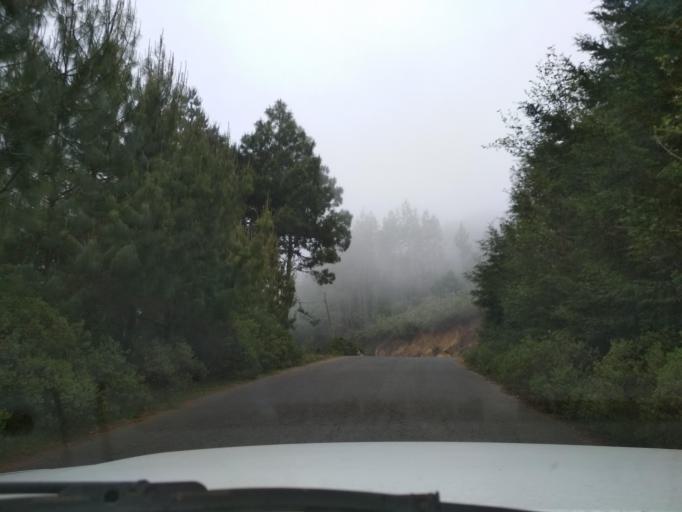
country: MX
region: Veracruz
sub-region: Mariano Escobedo
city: Loma Grande
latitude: 18.9307
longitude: -97.2212
